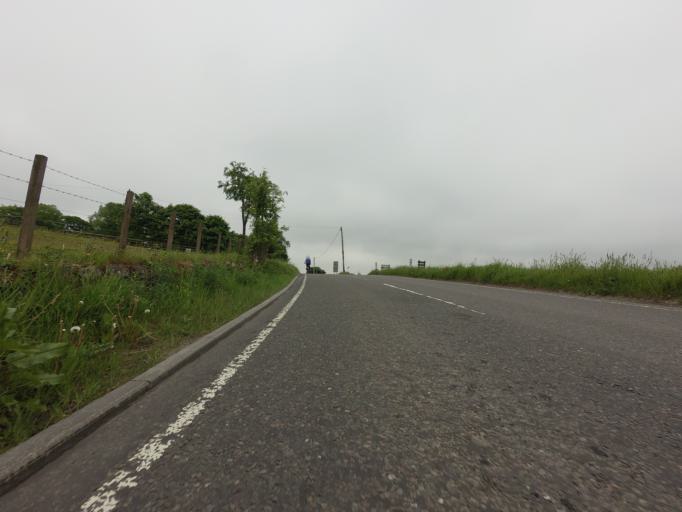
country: GB
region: Scotland
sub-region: Fife
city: Townhill
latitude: 56.1077
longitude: -3.4551
